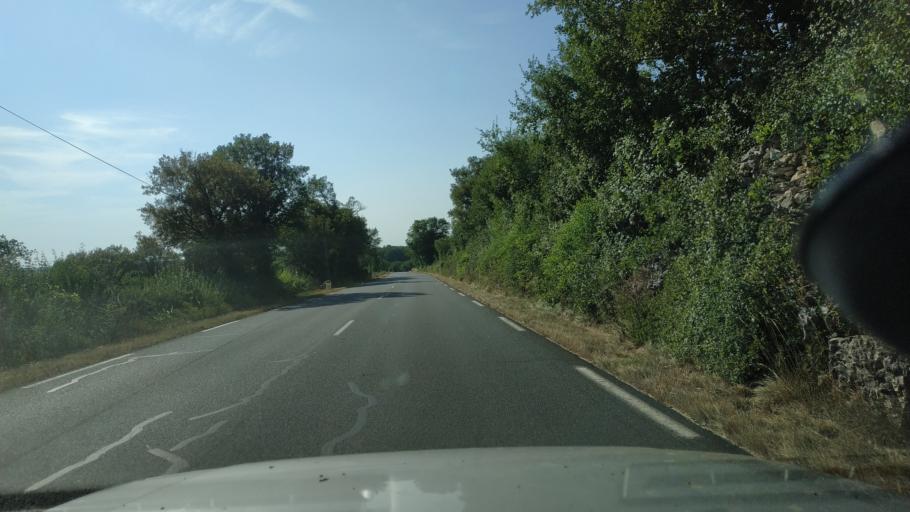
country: FR
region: Midi-Pyrenees
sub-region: Departement du Lot
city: Gramat
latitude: 44.7979
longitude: 1.6834
